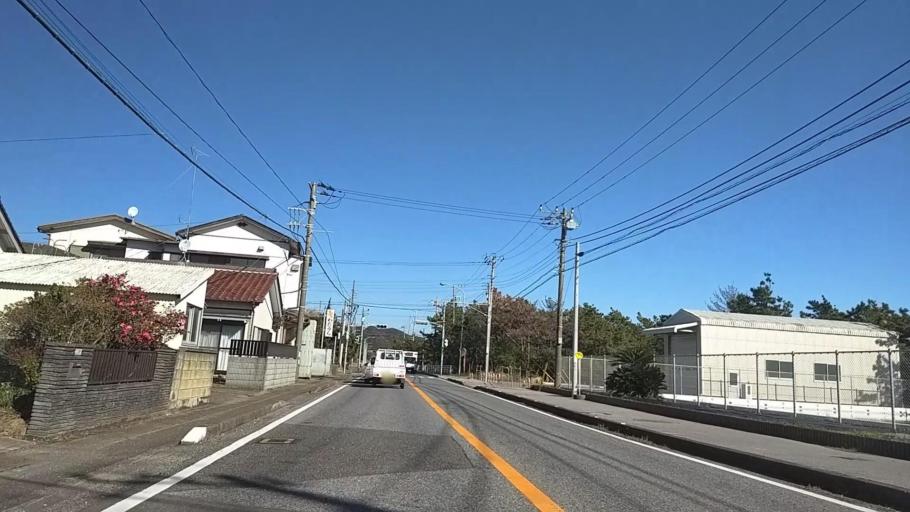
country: JP
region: Chiba
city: Kawaguchi
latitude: 35.0421
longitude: 140.0212
